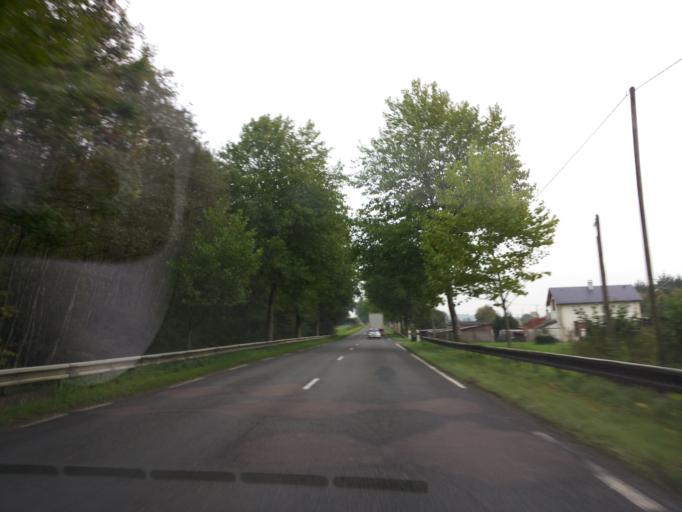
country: FR
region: Champagne-Ardenne
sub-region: Departement des Ardennes
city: Pouru-Saint-Remy
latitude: 49.6751
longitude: 5.0973
